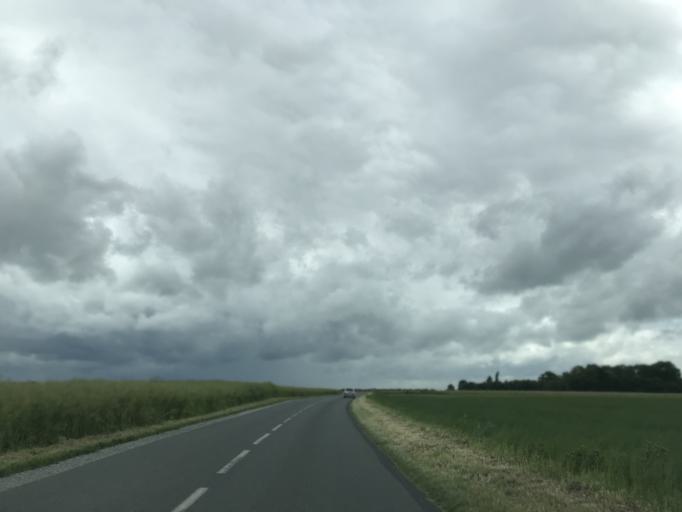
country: FR
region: Haute-Normandie
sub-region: Departement de l'Eure
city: Bueil
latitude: 48.9417
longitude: 1.4729
